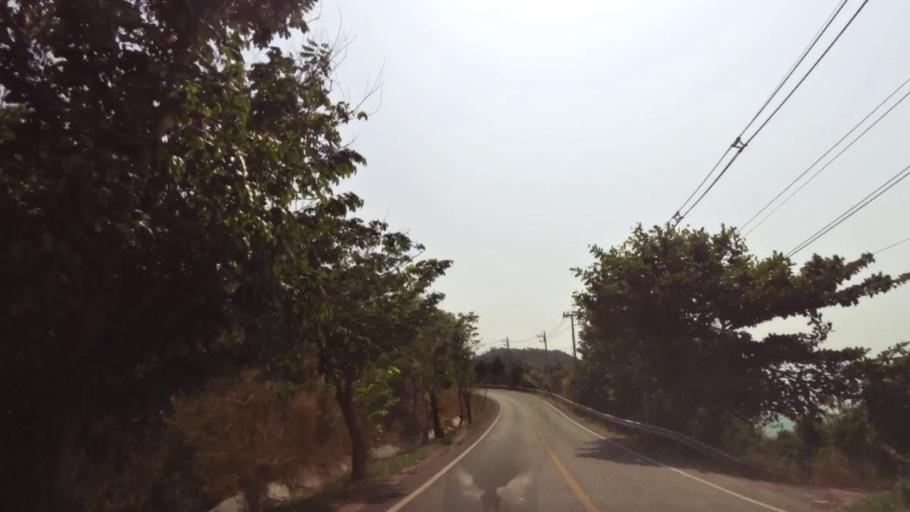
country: TH
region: Chanthaburi
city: Tha Mai
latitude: 12.5289
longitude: 101.9463
